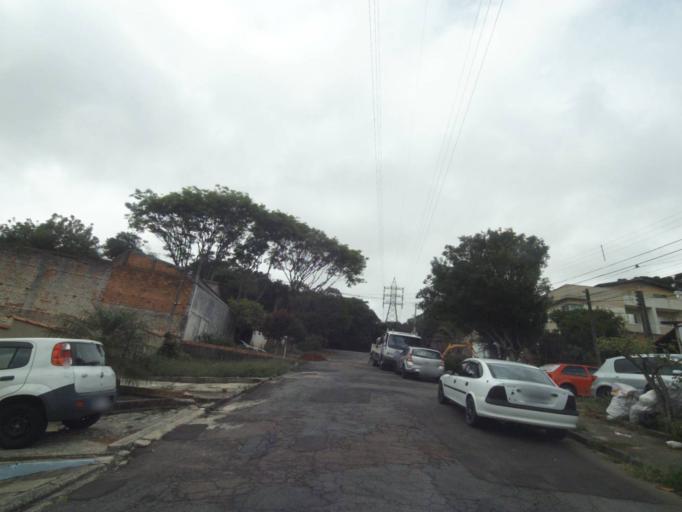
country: BR
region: Parana
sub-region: Curitiba
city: Curitiba
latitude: -25.3931
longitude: -49.2812
